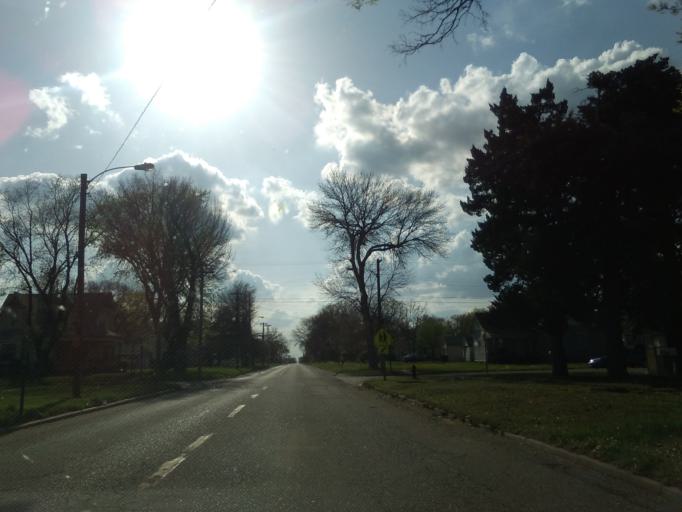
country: US
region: Nebraska
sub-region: Webster County
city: Red Cloud
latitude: 40.0888
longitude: -98.5256
